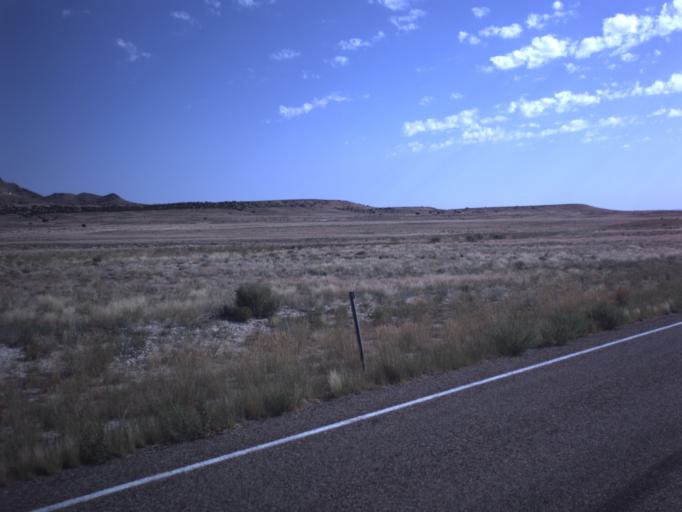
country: US
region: Utah
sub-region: Beaver County
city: Milford
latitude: 38.8110
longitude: -112.8711
